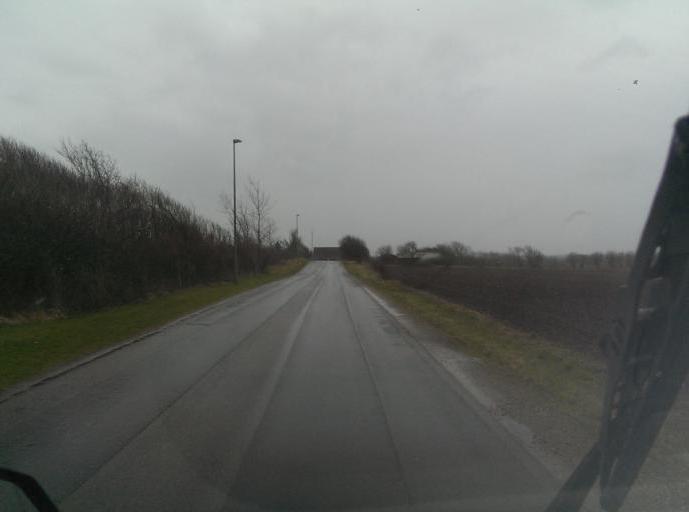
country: DK
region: Central Jutland
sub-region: Ringkobing-Skjern Kommune
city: Skjern
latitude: 56.0068
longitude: 8.4173
